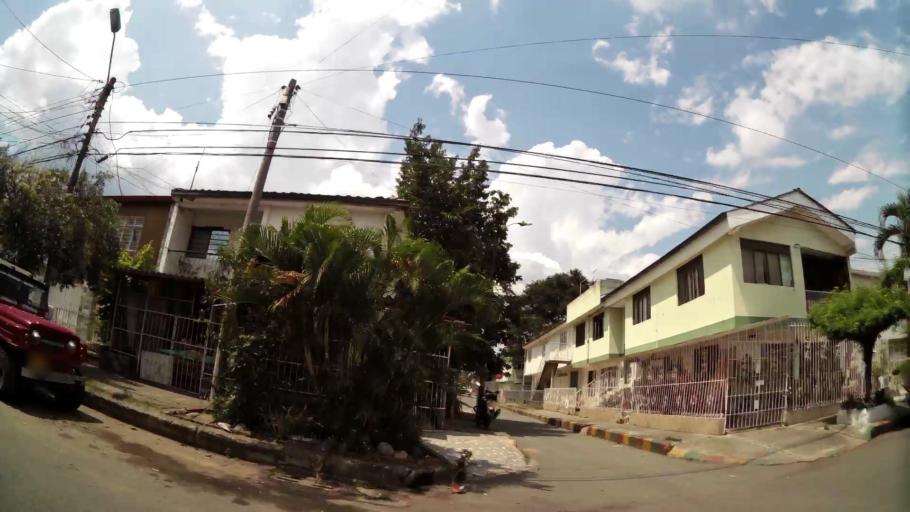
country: CO
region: Valle del Cauca
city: Cali
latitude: 3.4698
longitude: -76.5039
